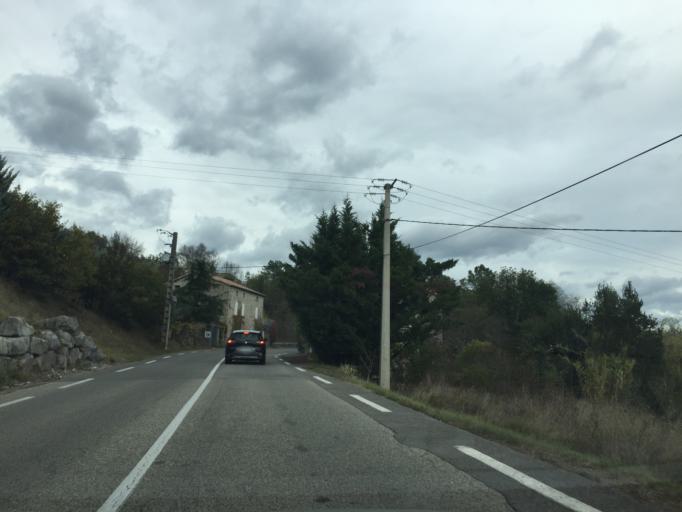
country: FR
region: Rhone-Alpes
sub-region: Departement de l'Ardeche
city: Lablachere
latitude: 44.4499
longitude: 4.2110
